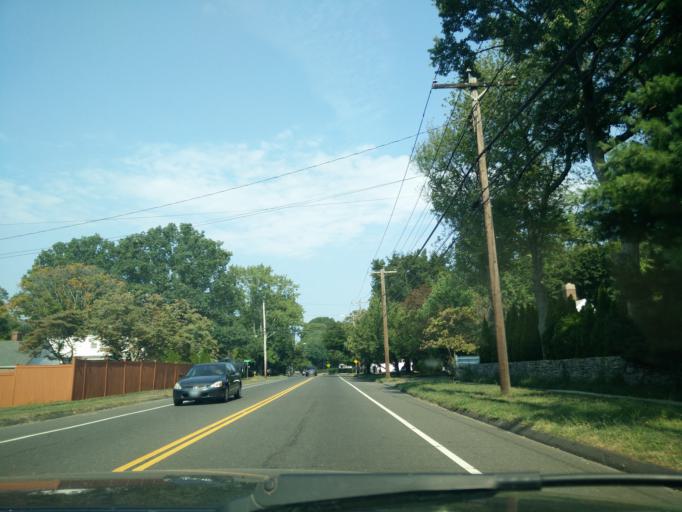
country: US
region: Connecticut
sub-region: Fairfield County
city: Bridgeport
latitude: 41.1947
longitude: -73.2296
